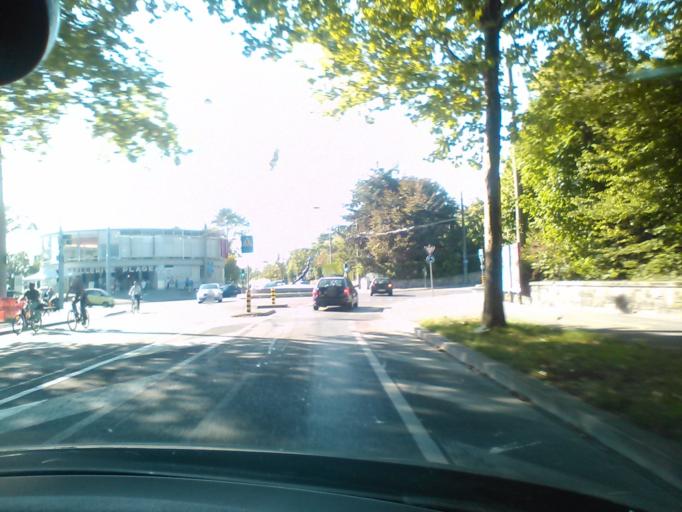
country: CH
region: Vaud
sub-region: Lausanne District
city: Lausanne
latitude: 46.5115
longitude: 6.6180
